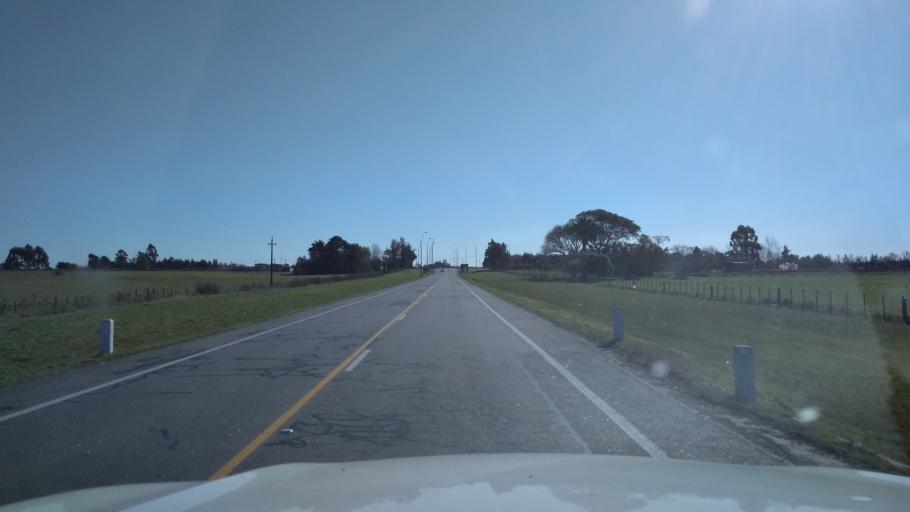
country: UY
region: Canelones
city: San Jacinto
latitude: -34.5302
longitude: -55.9477
